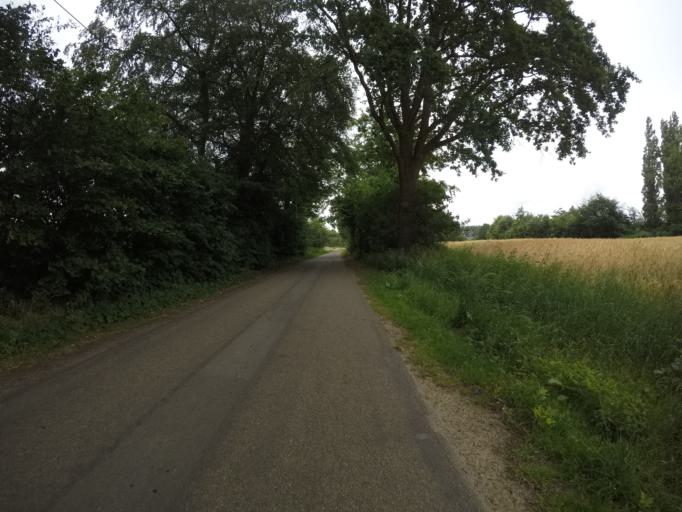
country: DE
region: North Rhine-Westphalia
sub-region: Regierungsbezirk Munster
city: Isselburg
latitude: 51.8558
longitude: 6.4373
